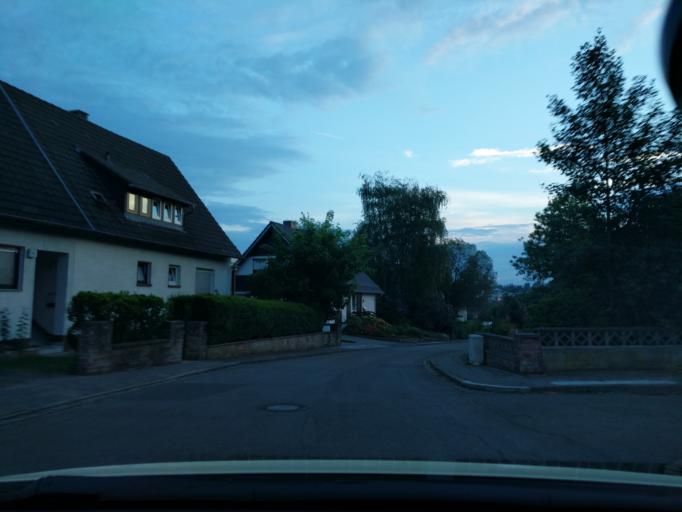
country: DE
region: Rheinland-Pfalz
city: Kaiserslautern
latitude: 49.4448
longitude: 7.7405
